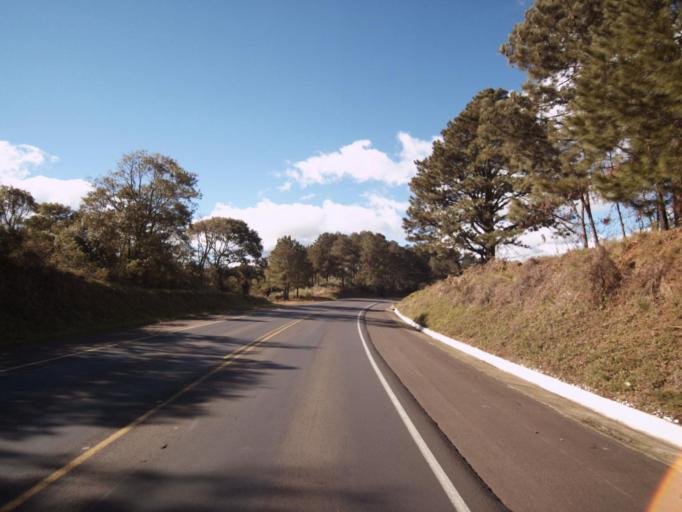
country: BR
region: Santa Catarina
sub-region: Joacaba
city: Joacaba
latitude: -26.9758
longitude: -51.7806
